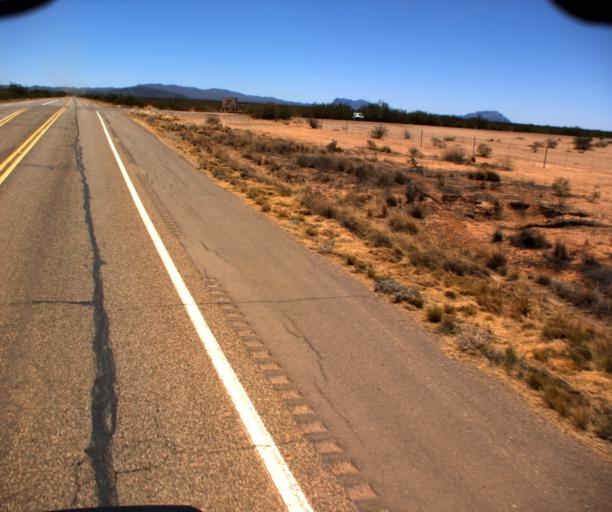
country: US
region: Arizona
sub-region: Pima County
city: Ajo
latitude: 32.1839
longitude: -112.3587
